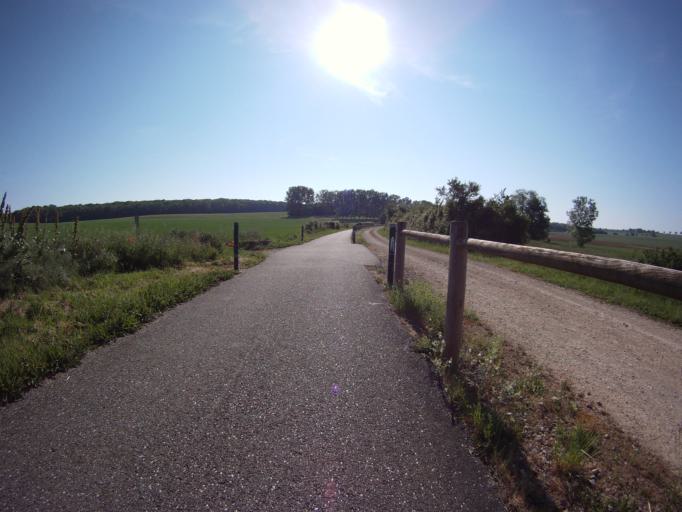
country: FR
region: Lorraine
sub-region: Departement de Meurthe-et-Moselle
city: Champenoux
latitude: 48.7420
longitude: 6.3014
